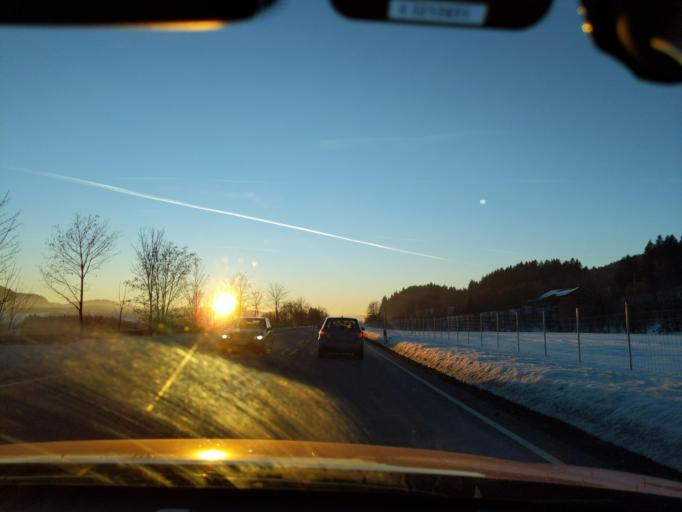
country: DE
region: Bavaria
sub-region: Swabia
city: Weitnau
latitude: 47.6576
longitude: 10.1721
